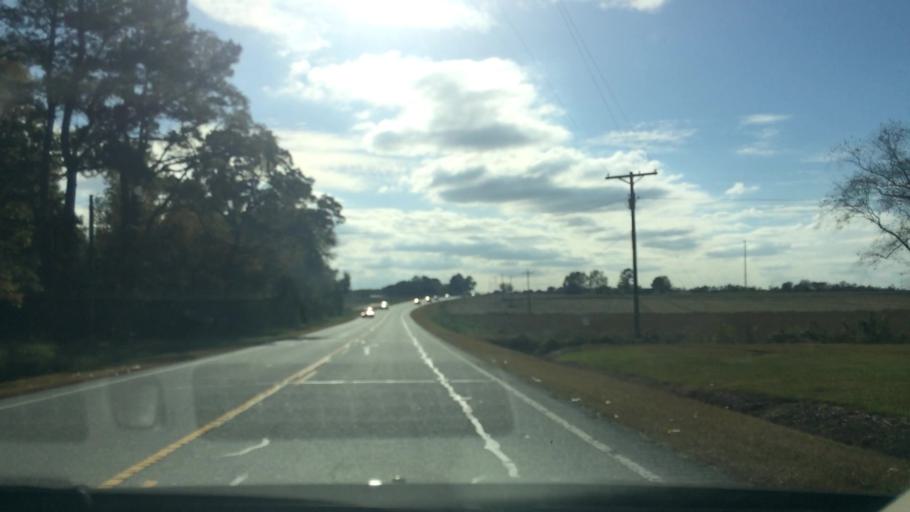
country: US
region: North Carolina
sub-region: Greene County
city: Snow Hill
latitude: 35.4507
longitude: -77.7325
